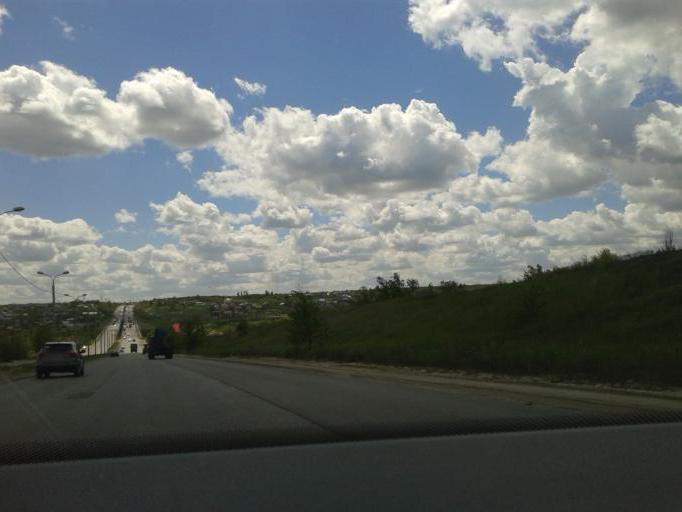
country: RU
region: Volgograd
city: Volgograd
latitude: 48.7233
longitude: 44.4462
